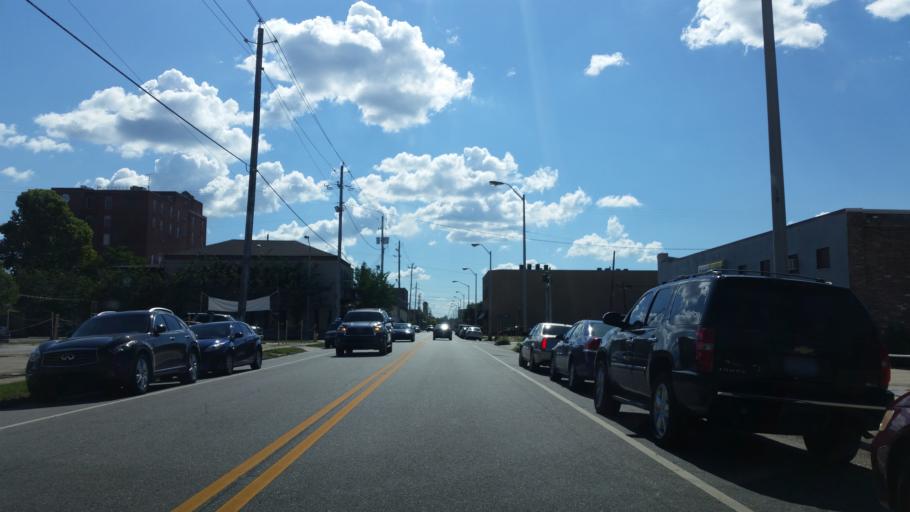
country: US
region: Alabama
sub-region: Mobile County
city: Mobile
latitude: 30.6936
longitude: -88.0453
